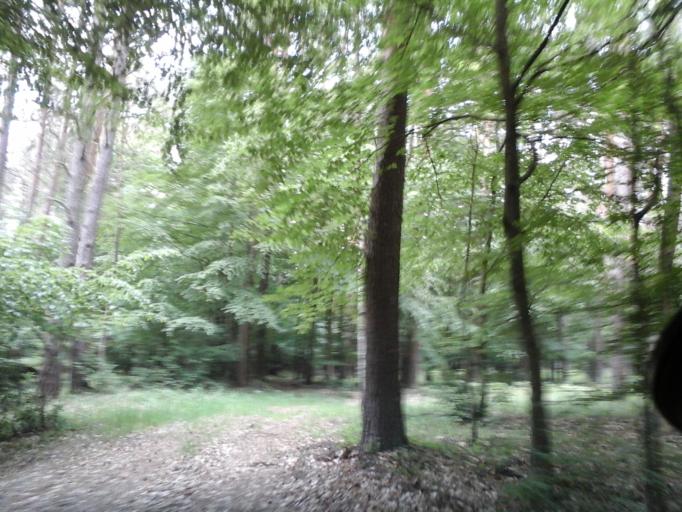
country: PL
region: West Pomeranian Voivodeship
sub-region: Powiat choszczenski
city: Drawno
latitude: 53.1198
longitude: 15.8786
